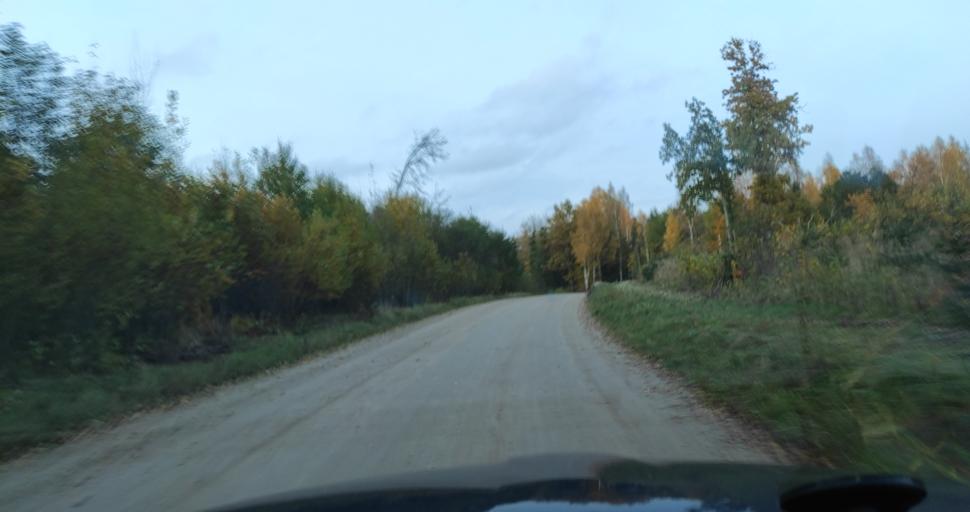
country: LV
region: Vainode
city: Vainode
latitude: 56.6347
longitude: 21.8124
